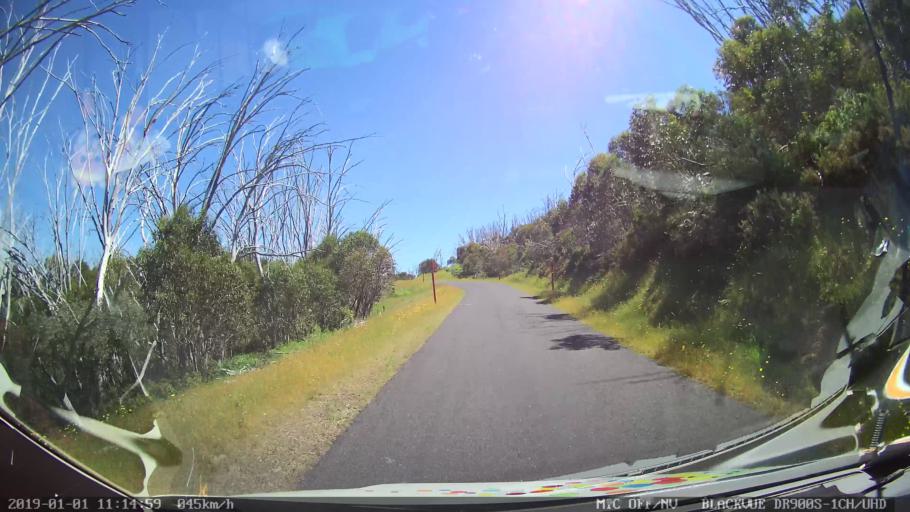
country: AU
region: New South Wales
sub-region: Snowy River
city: Jindabyne
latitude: -35.9480
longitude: 148.3868
